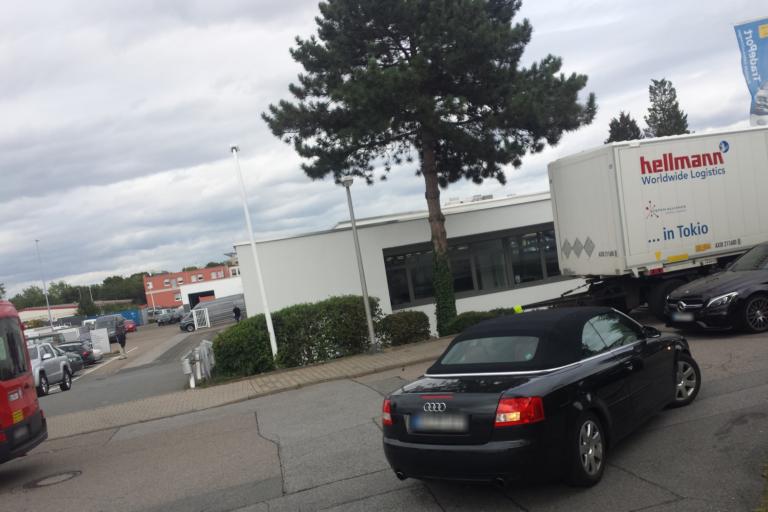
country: DE
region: Baden-Wuerttemberg
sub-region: Karlsruhe Region
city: Mannheim
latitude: 49.5076
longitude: 8.5260
